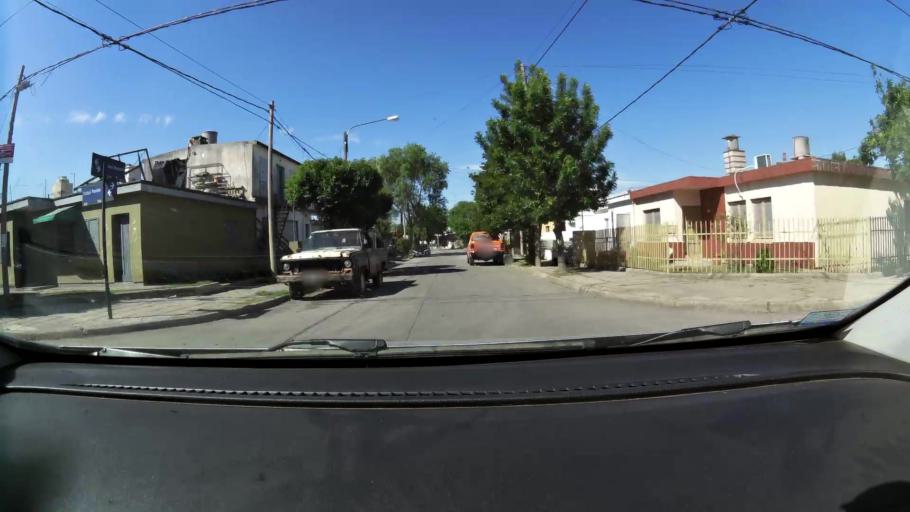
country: AR
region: Cordoba
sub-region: Departamento de Capital
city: Cordoba
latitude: -31.3631
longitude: -64.1671
